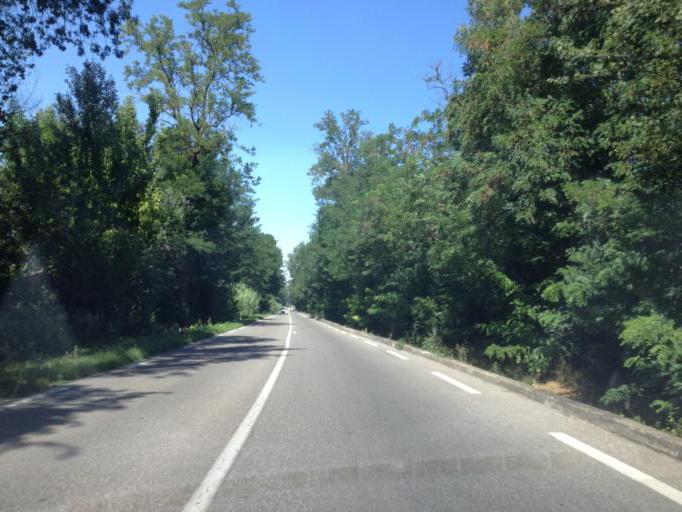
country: FR
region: Languedoc-Roussillon
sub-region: Departement du Gard
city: Roquemaure
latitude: 44.0611
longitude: 4.7705
